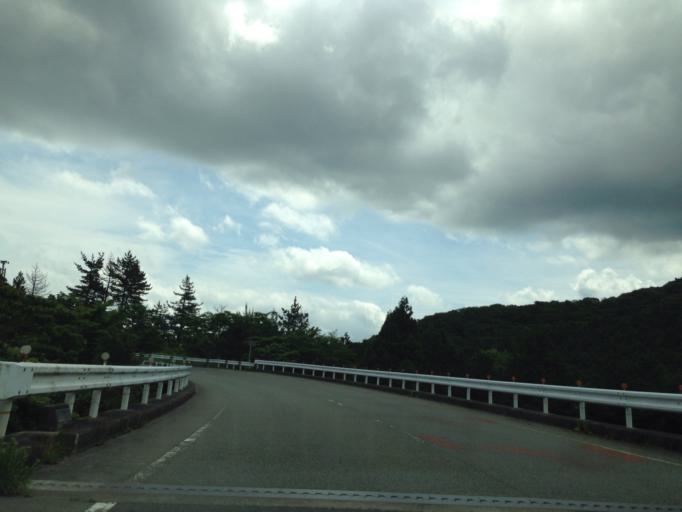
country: JP
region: Shizuoka
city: Heda
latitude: 34.9196
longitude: 138.8576
